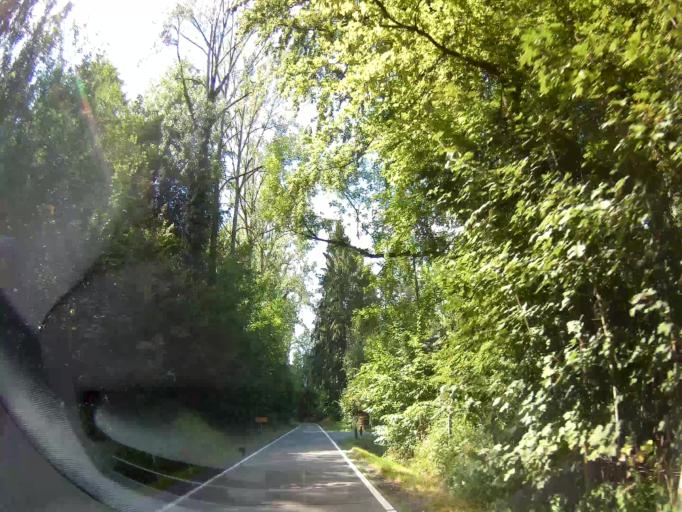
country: BE
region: Wallonia
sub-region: Province de Namur
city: Yvoir
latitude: 50.3532
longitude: 4.9217
